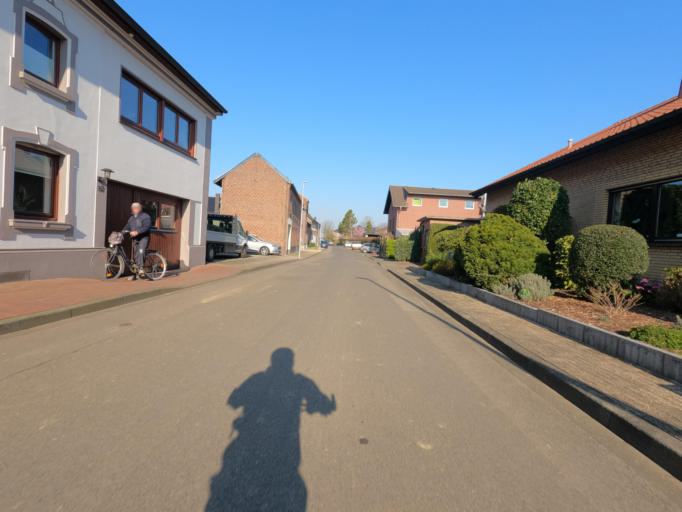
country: DE
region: North Rhine-Westphalia
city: Erkelenz
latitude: 51.1030
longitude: 6.2863
